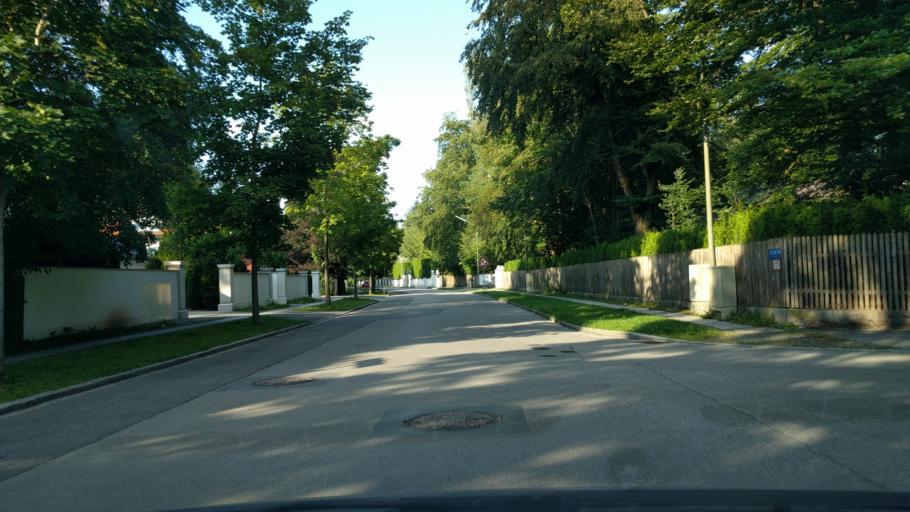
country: DE
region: Bavaria
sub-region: Upper Bavaria
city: Pullach im Isartal
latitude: 48.0560
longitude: 11.5430
